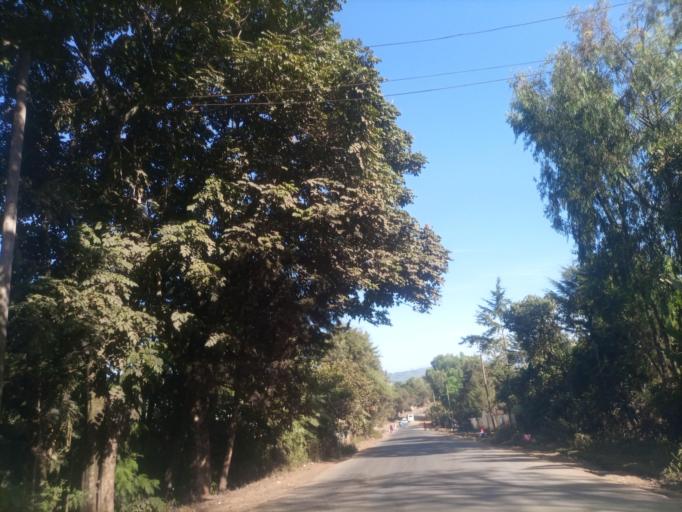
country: ET
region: Oromiya
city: Jima
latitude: 7.7001
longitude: 36.8116
